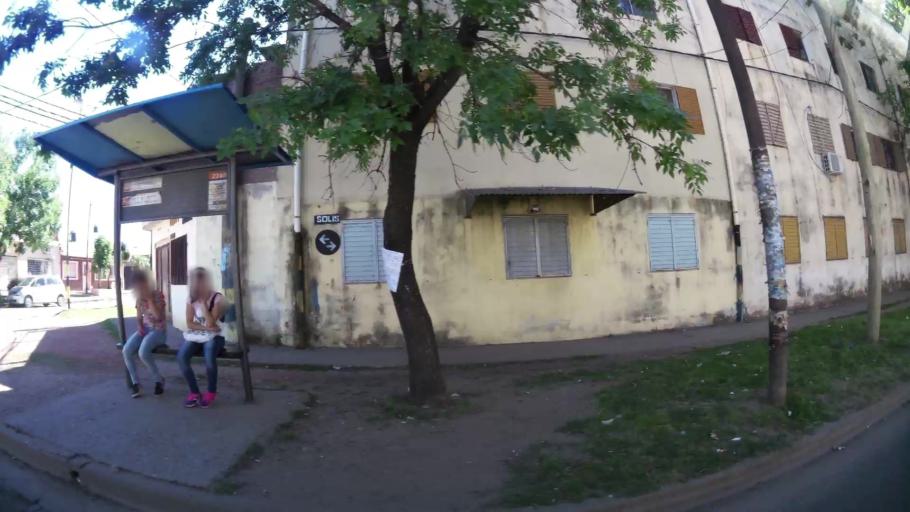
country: AR
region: Santa Fe
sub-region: Departamento de Rosario
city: Rosario
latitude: -32.9311
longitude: -60.7039
